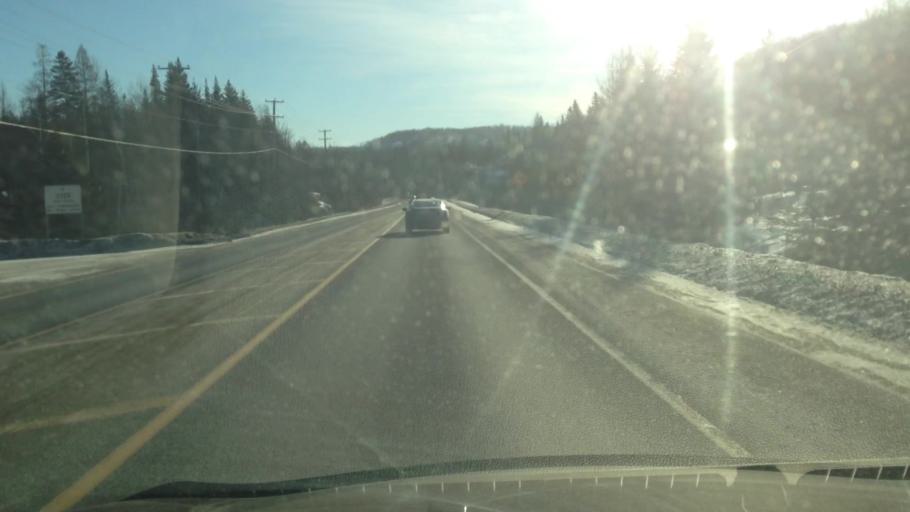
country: CA
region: Quebec
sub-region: Laurentides
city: Saint-Sauveur
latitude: 45.8892
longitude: -74.1908
